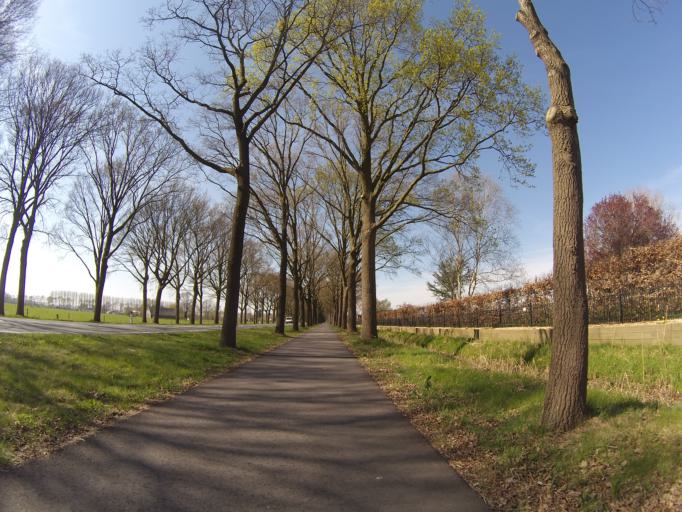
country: NL
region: Gelderland
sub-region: Gemeente Ede
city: Ederveen
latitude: 52.0522
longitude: 5.5679
